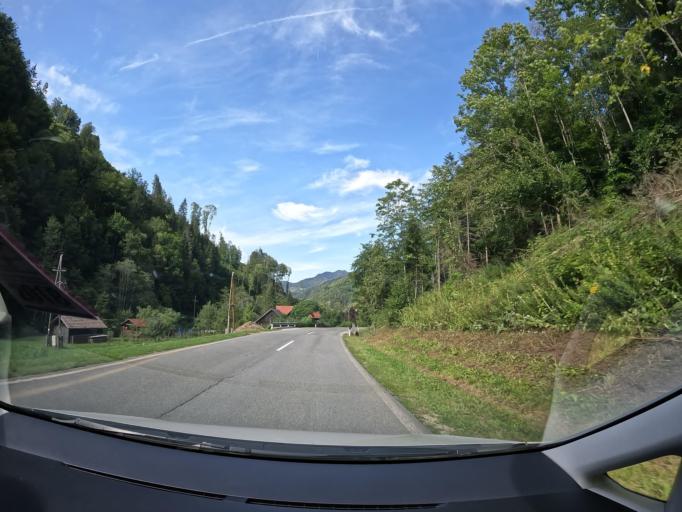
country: AT
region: Carinthia
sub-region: Politischer Bezirk Volkermarkt
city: Bad Eisenkappel
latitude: 46.4634
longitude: 14.5893
